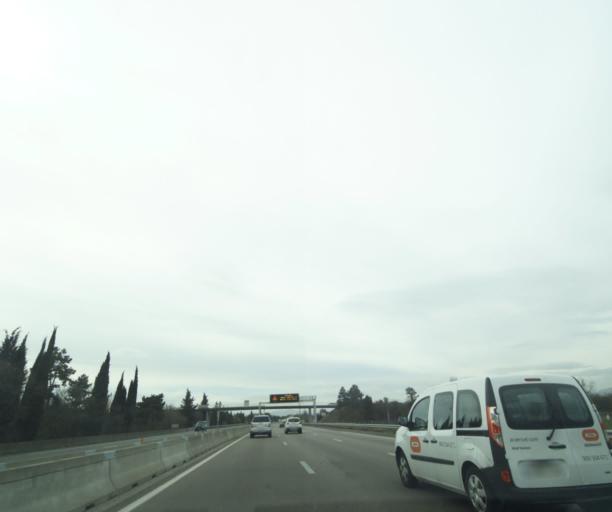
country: FR
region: Rhone-Alpes
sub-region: Departement de la Drome
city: Livron-sur-Drome
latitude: 44.7912
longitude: 4.8396
